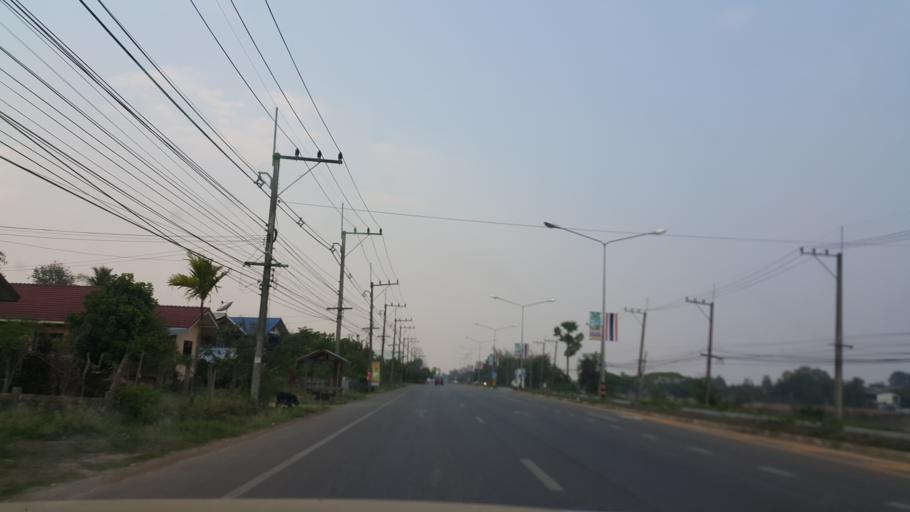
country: TH
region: Nakhon Phanom
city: That Phanom
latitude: 16.9966
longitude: 104.7235
